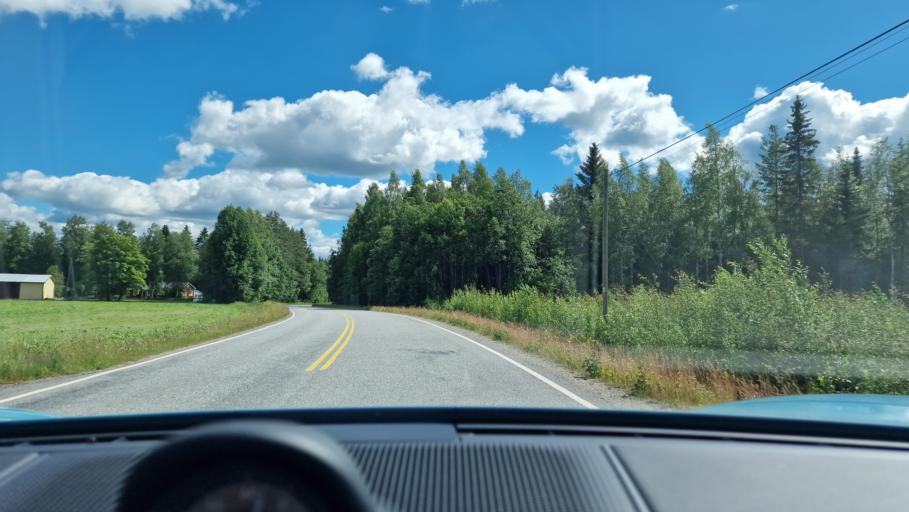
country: FI
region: Southern Ostrobothnia
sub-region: Jaerviseutu
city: Soini
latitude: 62.8296
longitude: 24.3392
